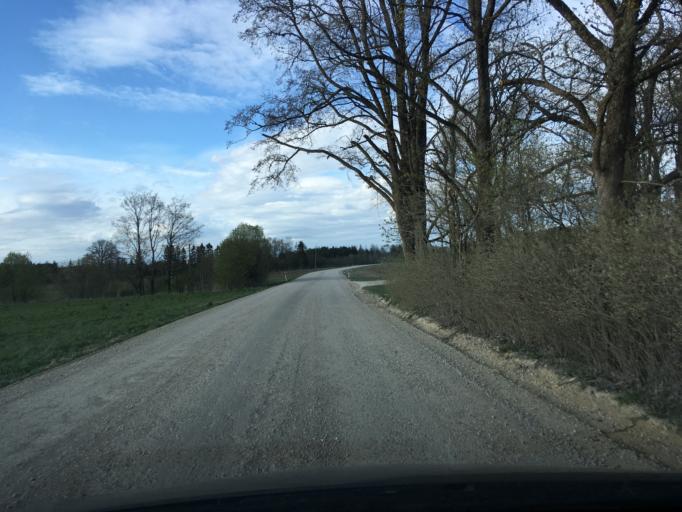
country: EE
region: Raplamaa
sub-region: Maerjamaa vald
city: Marjamaa
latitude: 58.9362
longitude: 24.3089
